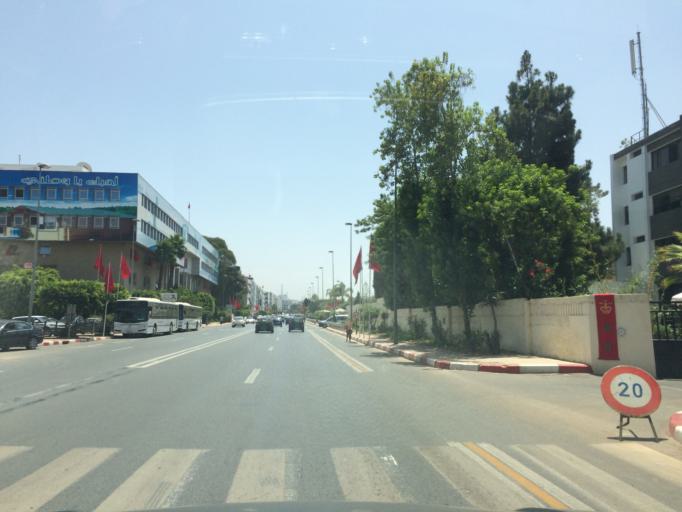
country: MA
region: Rabat-Sale-Zemmour-Zaer
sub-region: Rabat
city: Rabat
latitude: 33.9937
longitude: -6.8514
